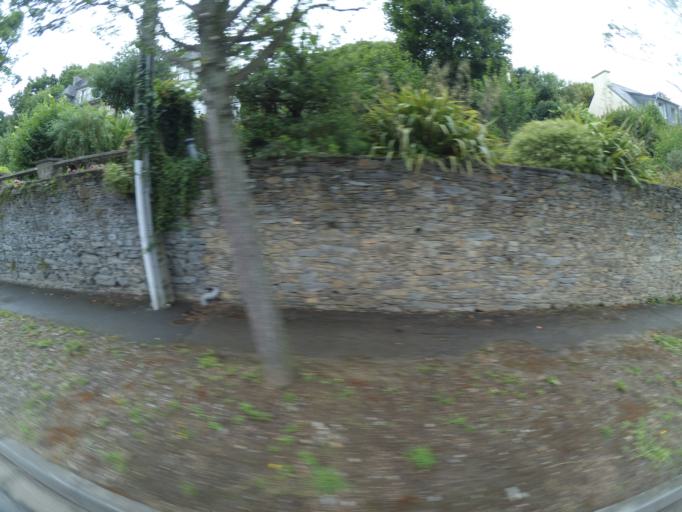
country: FR
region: Brittany
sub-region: Departement du Finistere
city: Morlaix
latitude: 48.5871
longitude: -3.8367
